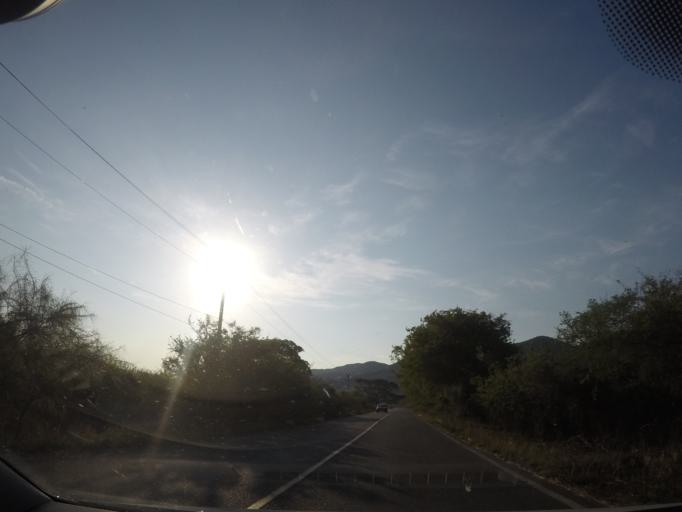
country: MX
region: Oaxaca
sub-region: Santo Domingo Tehuantepec
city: La Noria
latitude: 16.2309
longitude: -95.1809
